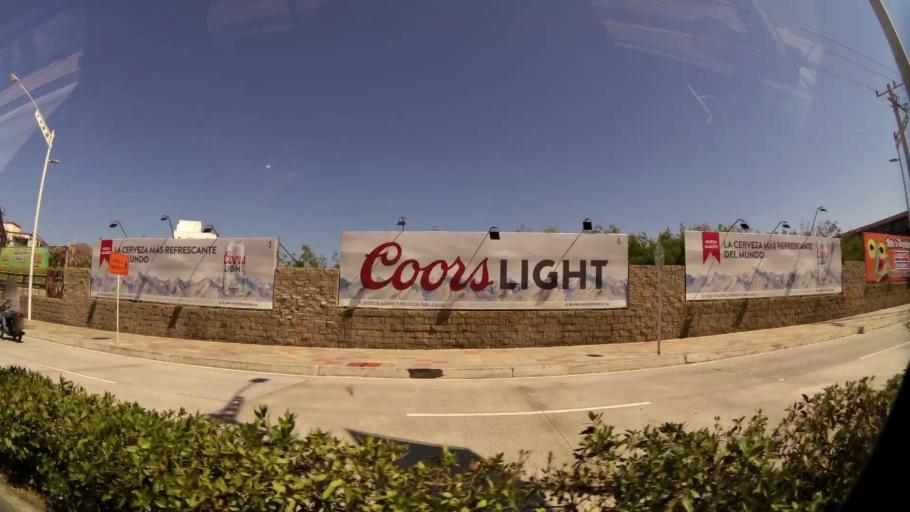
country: CO
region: Atlantico
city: Barranquilla
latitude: 11.0090
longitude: -74.8226
